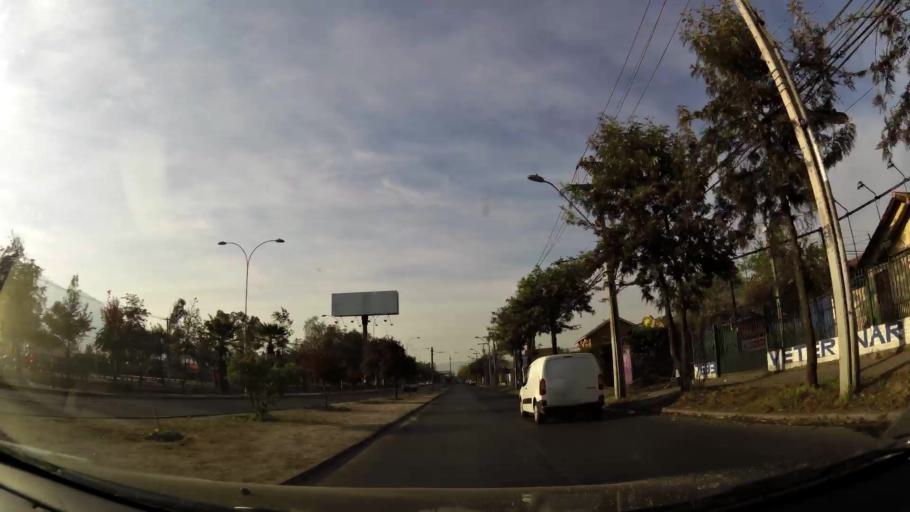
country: CL
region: Santiago Metropolitan
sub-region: Provincia de Santiago
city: Villa Presidente Frei, Nunoa, Santiago, Chile
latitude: -33.5246
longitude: -70.5781
